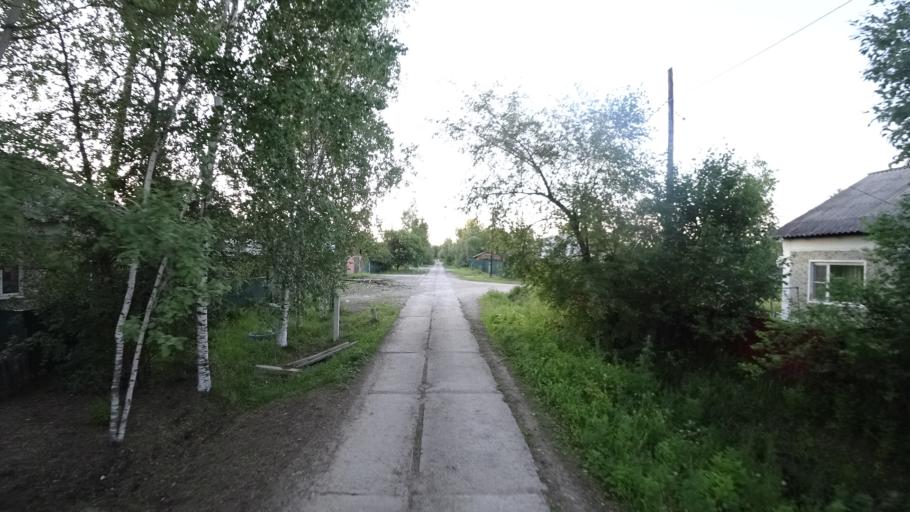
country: RU
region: Khabarovsk Krai
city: Khor
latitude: 47.8458
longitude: 134.9526
